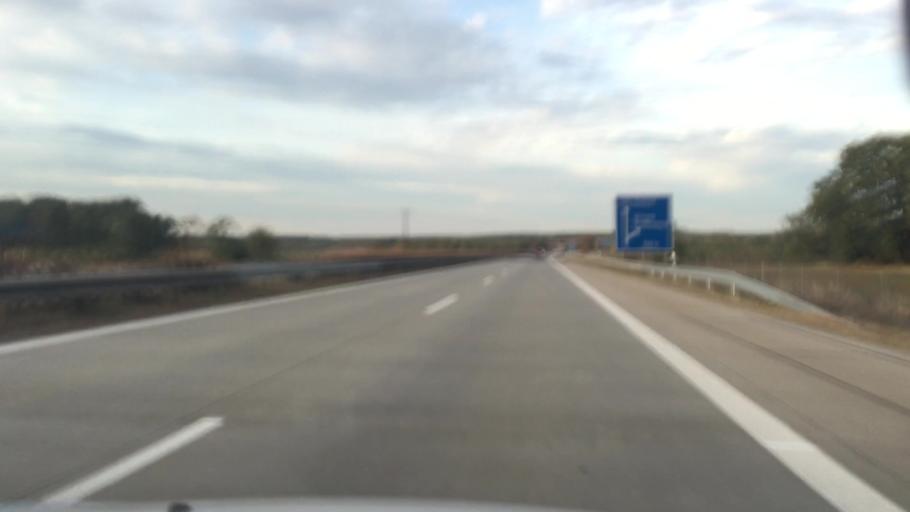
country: DE
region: Brandenburg
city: Ortrand
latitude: 51.3791
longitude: 13.7474
